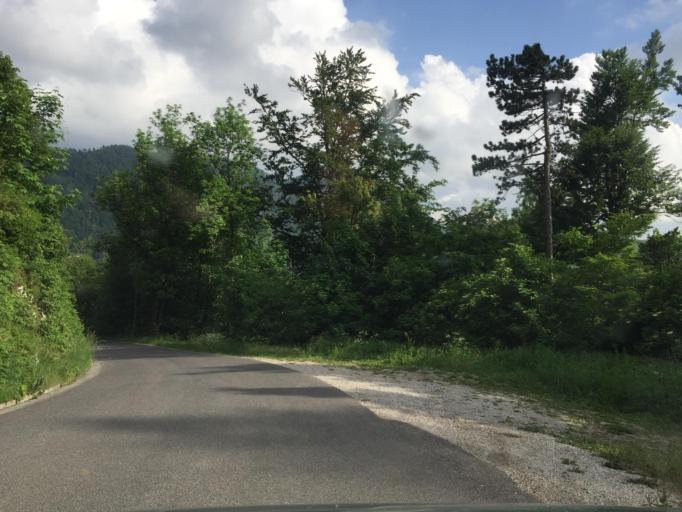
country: SI
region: Nova Gorica
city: Sempas
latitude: 46.0412
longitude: 13.7787
